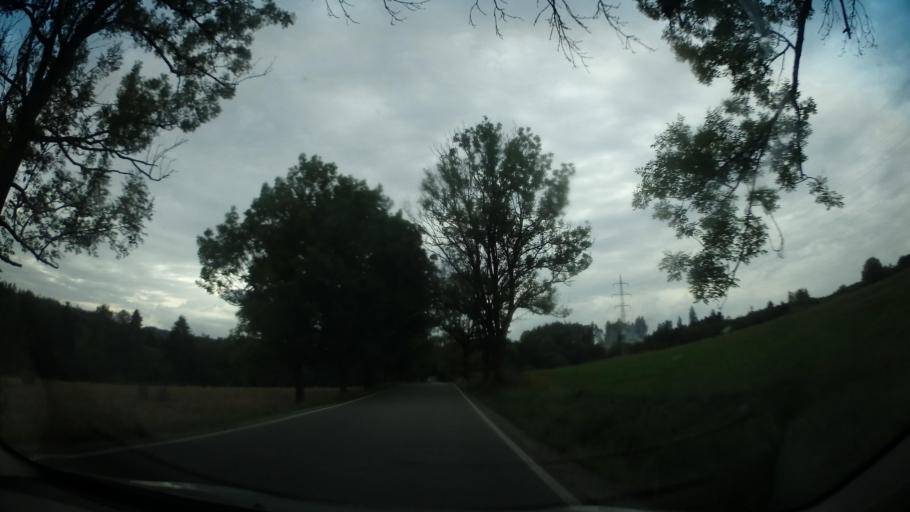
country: CZ
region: Pardubicky
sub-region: Okres Chrudim
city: Nasavrky
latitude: 49.7916
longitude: 15.8038
